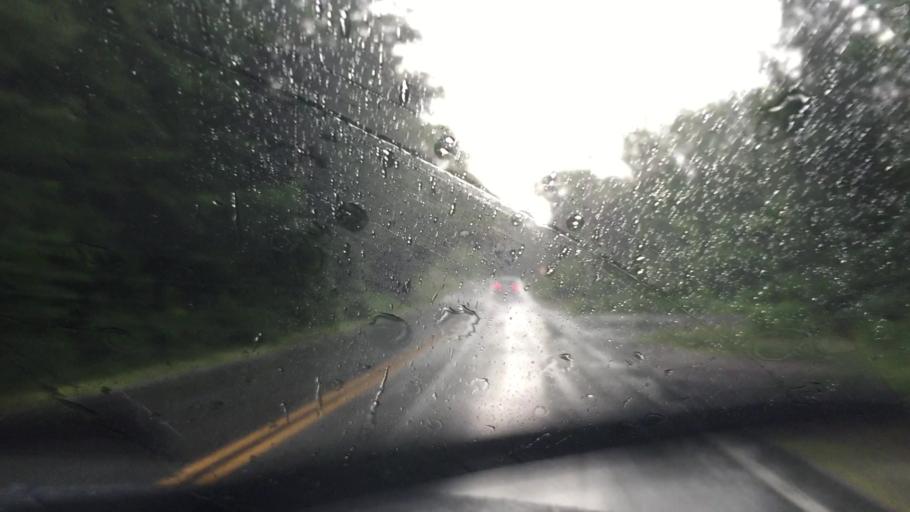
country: US
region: New Hampshire
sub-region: Grafton County
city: Holderness
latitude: 43.7211
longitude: -71.5466
